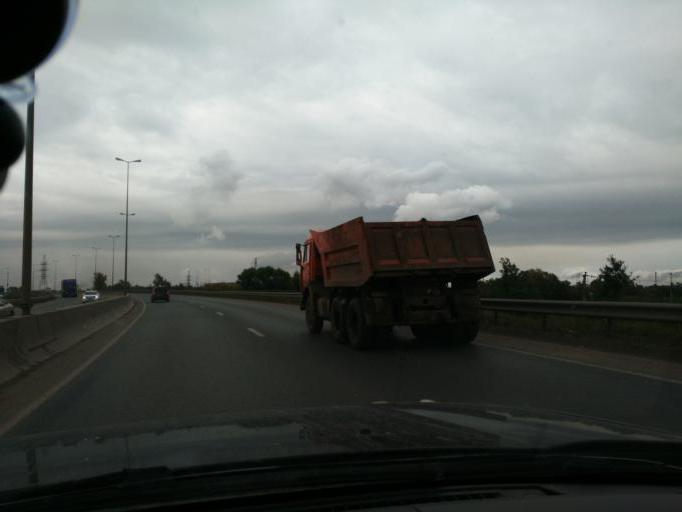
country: RU
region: Perm
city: Kondratovo
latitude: 57.9468
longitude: 56.1237
